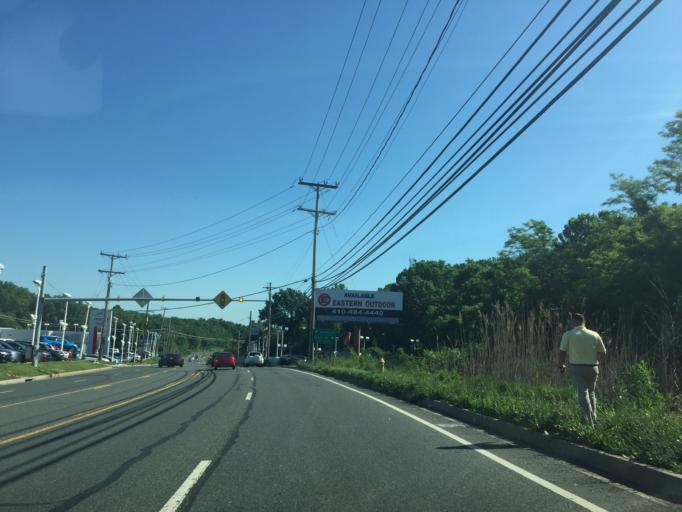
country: US
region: Maryland
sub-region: Harford County
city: Pleasant Hills
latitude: 39.5044
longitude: -76.3819
